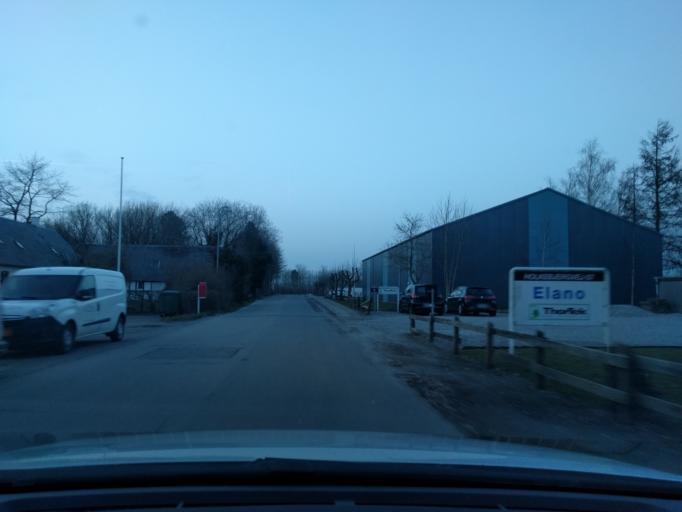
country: DK
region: South Denmark
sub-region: Odense Kommune
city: Bellinge
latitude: 55.3580
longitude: 10.3234
